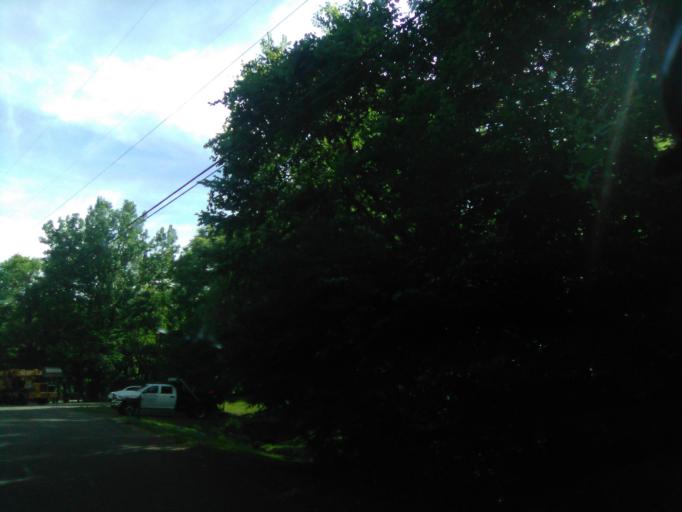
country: US
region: Tennessee
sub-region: Davidson County
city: Belle Meade
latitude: 36.1100
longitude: -86.9003
